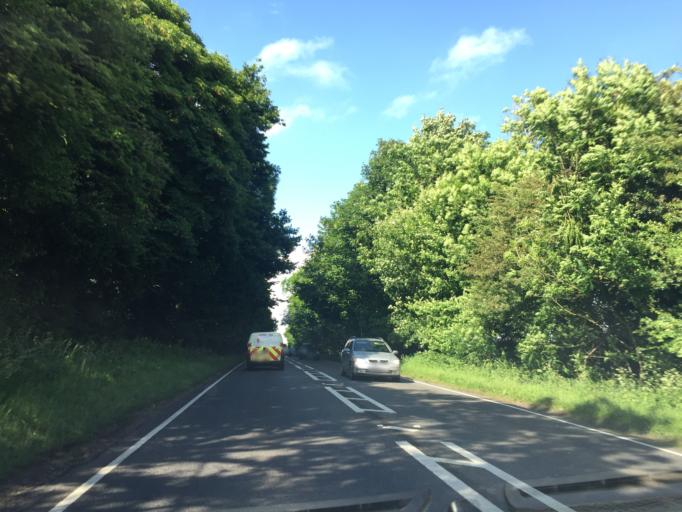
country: GB
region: England
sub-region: Dorset
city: Dorchester
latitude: 50.7266
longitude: -2.4078
